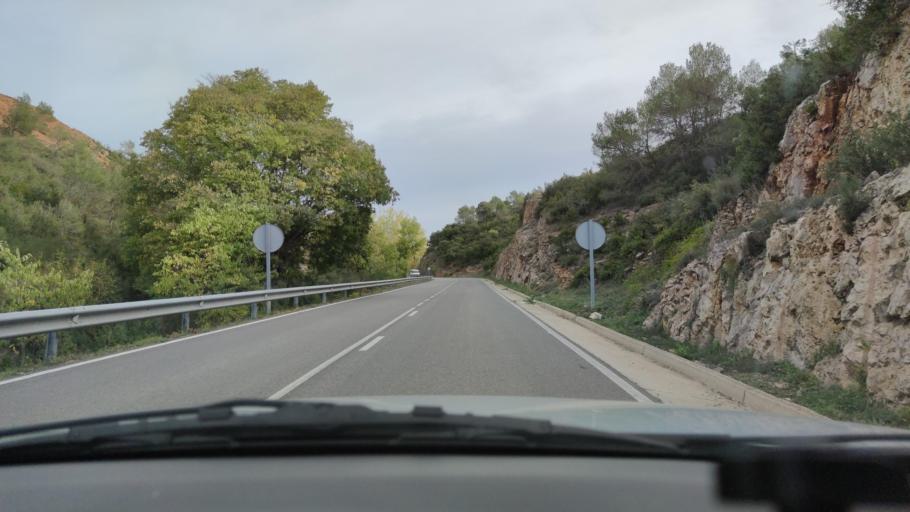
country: ES
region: Catalonia
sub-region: Provincia de Lleida
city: Artesa de Segre
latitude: 41.9333
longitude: 1.0521
